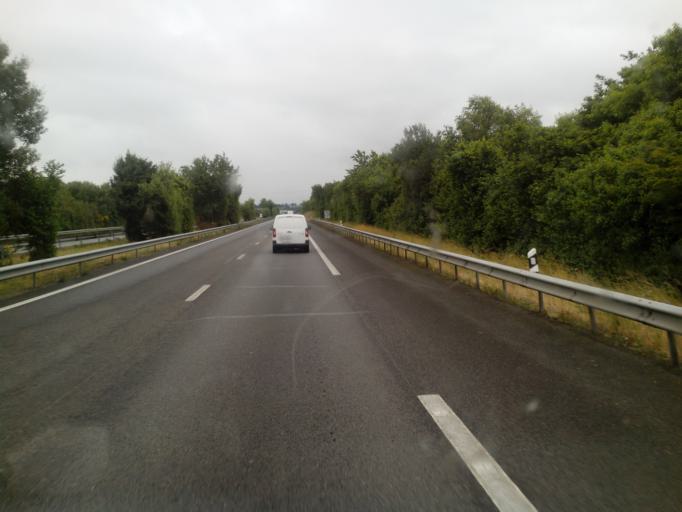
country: FR
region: Brittany
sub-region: Departement d'Ille-et-Vilaine
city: Crevin
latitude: 47.9502
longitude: -1.6788
